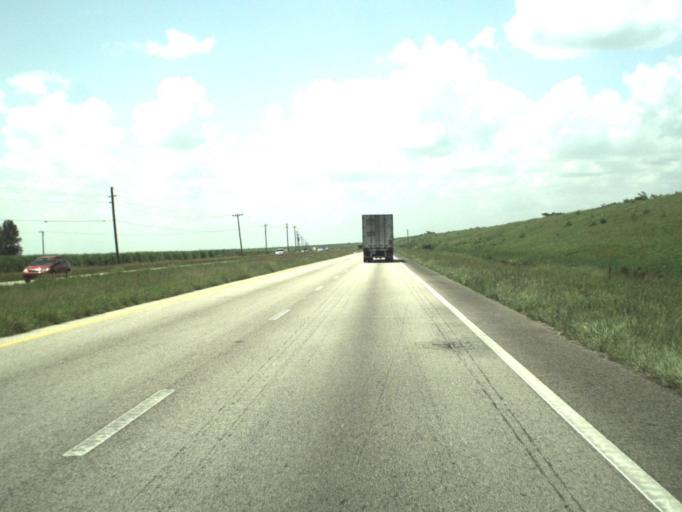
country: US
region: Florida
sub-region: Palm Beach County
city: South Bay
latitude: 26.6923
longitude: -80.7695
